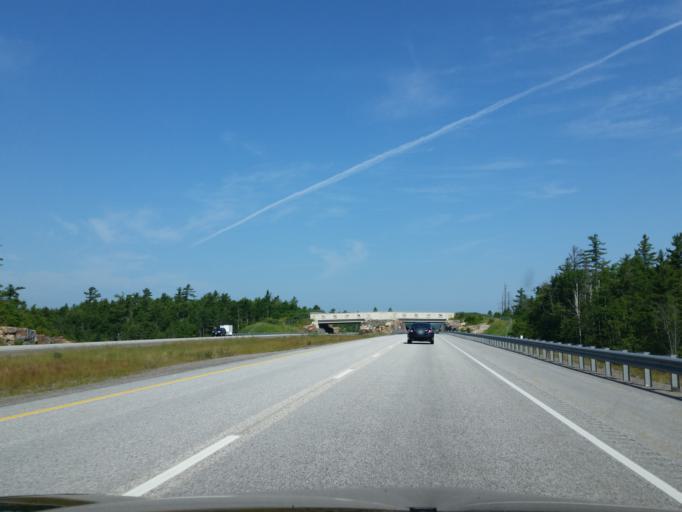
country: CA
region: Ontario
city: Greater Sudbury
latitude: 46.2354
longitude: -80.7801
